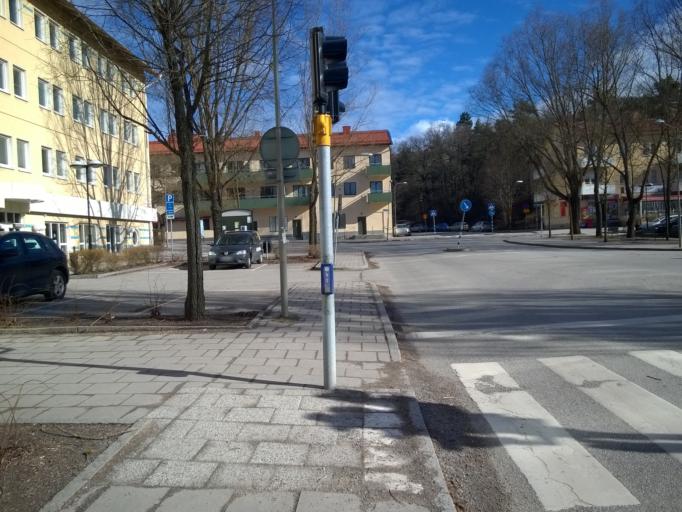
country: SE
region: Stockholm
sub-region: Sundbybergs Kommun
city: Sundbyberg
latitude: 59.3350
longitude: 17.9783
